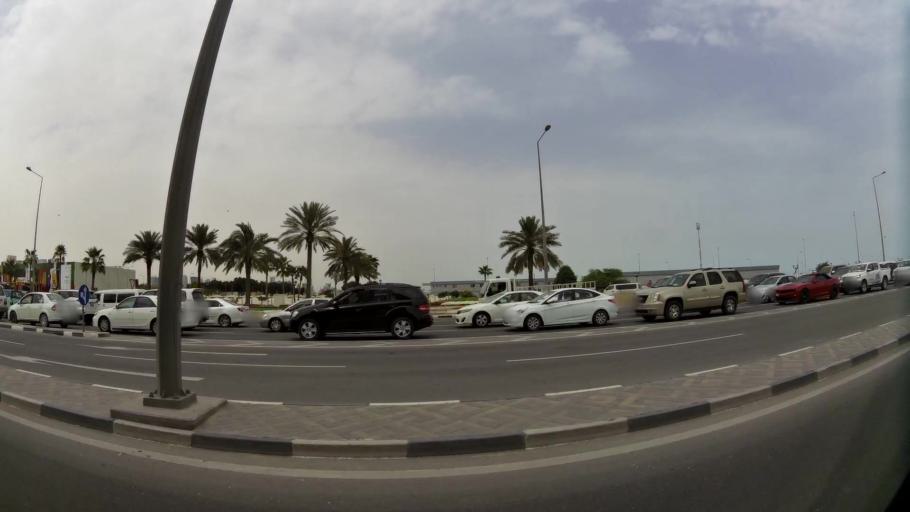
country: QA
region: Baladiyat ad Dawhah
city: Doha
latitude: 25.2912
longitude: 51.5447
